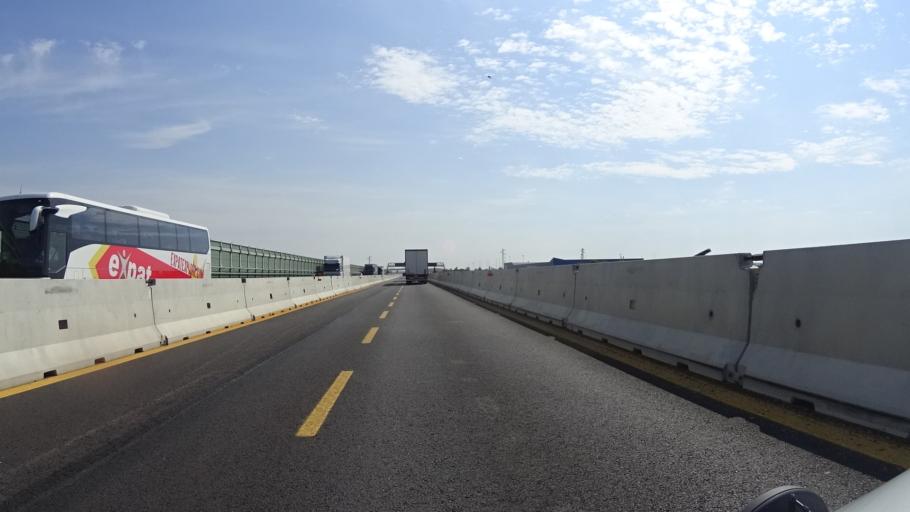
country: IT
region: Friuli Venezia Giulia
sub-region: Provincia di Udine
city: Teor
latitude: 45.8200
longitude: 13.0355
